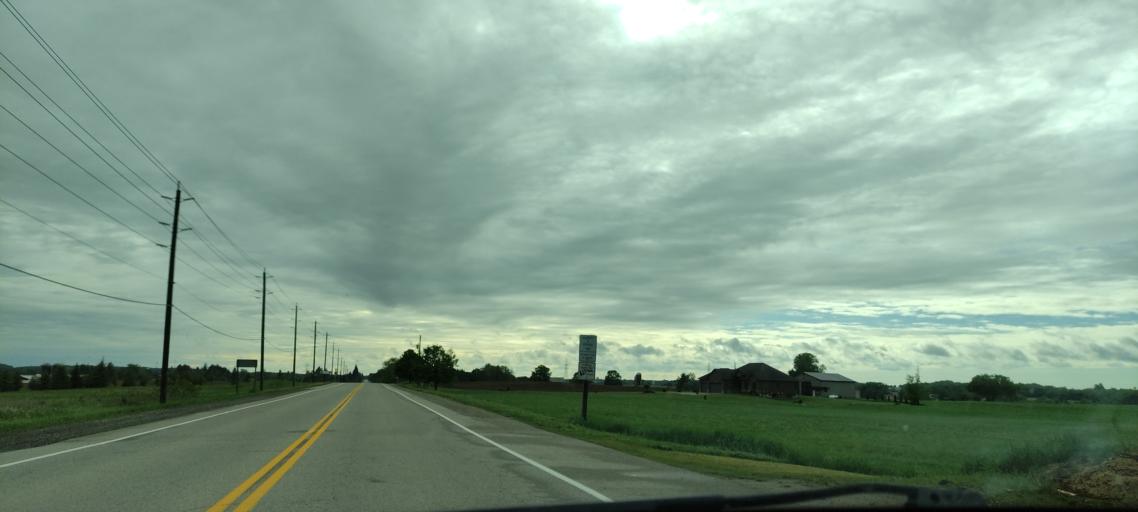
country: CA
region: Ontario
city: Kitchener
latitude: 43.3832
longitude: -80.6444
